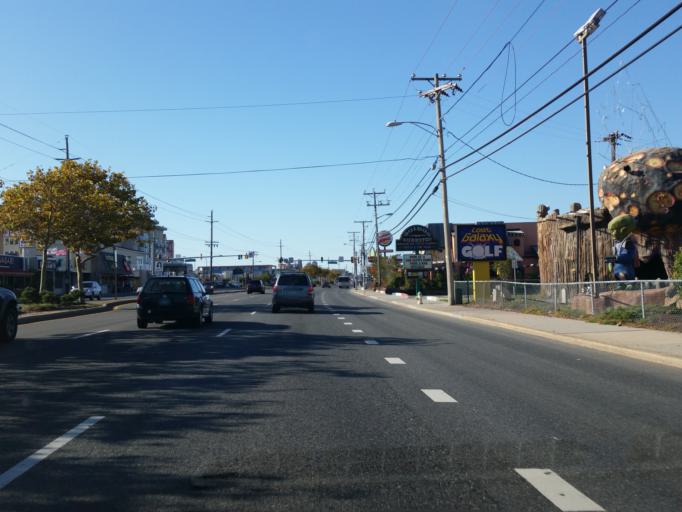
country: US
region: Maryland
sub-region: Worcester County
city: Ocean City
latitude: 38.3628
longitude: -75.0727
